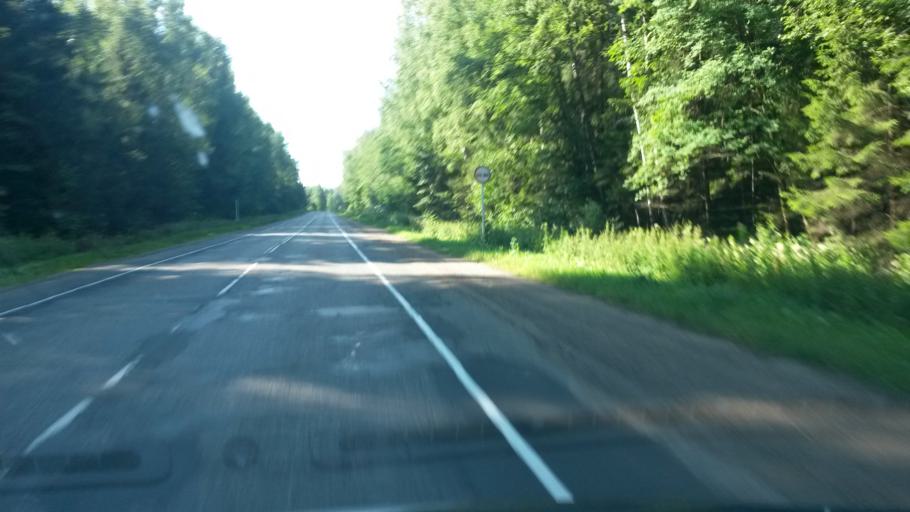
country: RU
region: Ivanovo
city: Pistsovo
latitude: 57.1130
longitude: 40.6478
